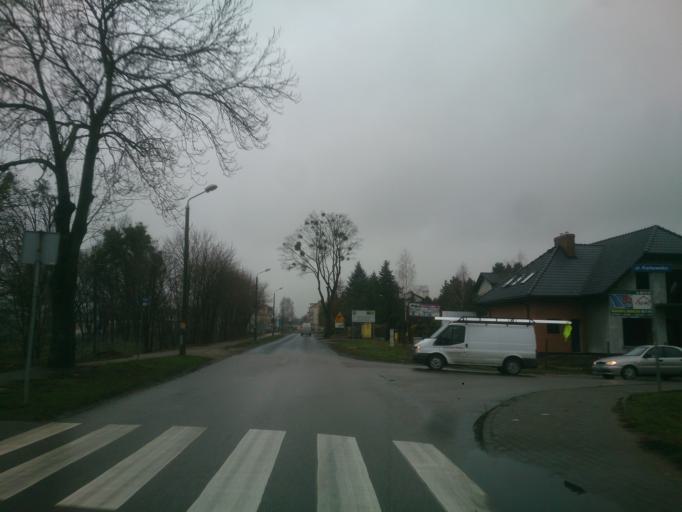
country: PL
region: Kujawsko-Pomorskie
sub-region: Powiat brodnicki
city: Brodnica
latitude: 53.2677
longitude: 19.3909
